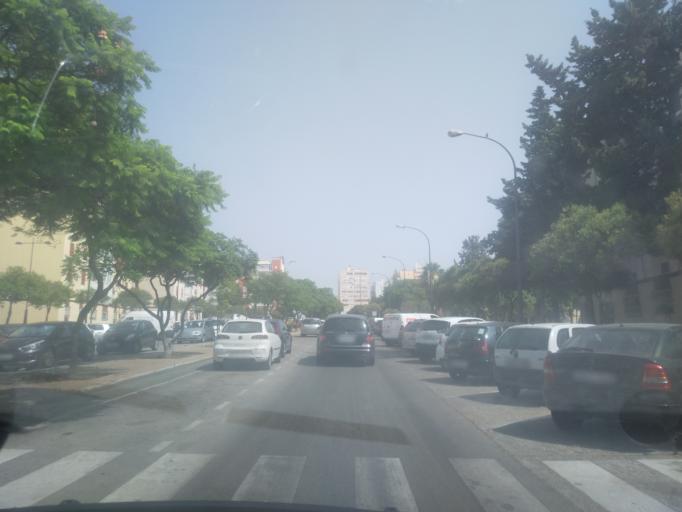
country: ES
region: Andalusia
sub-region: Provincia de Cadiz
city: San Fernando
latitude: 36.4713
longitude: -6.2015
